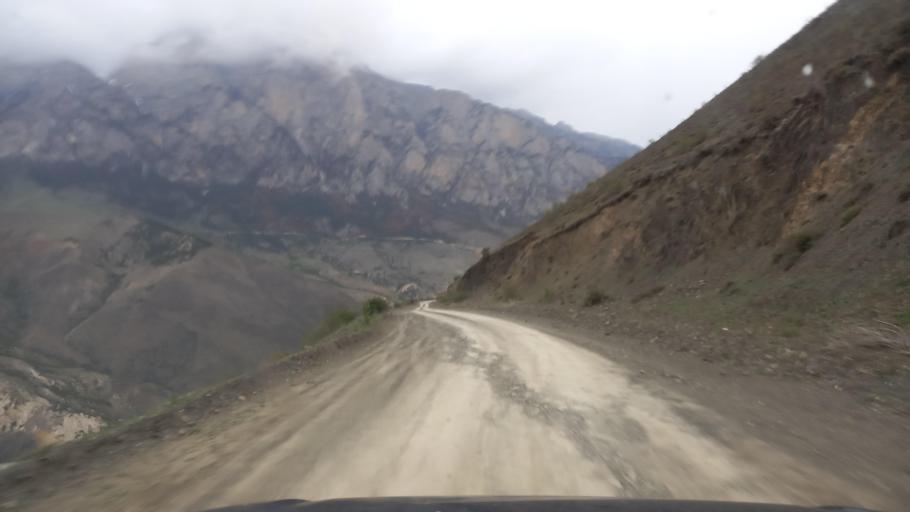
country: RU
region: North Ossetia
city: Mizur
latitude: 42.8563
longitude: 44.1597
